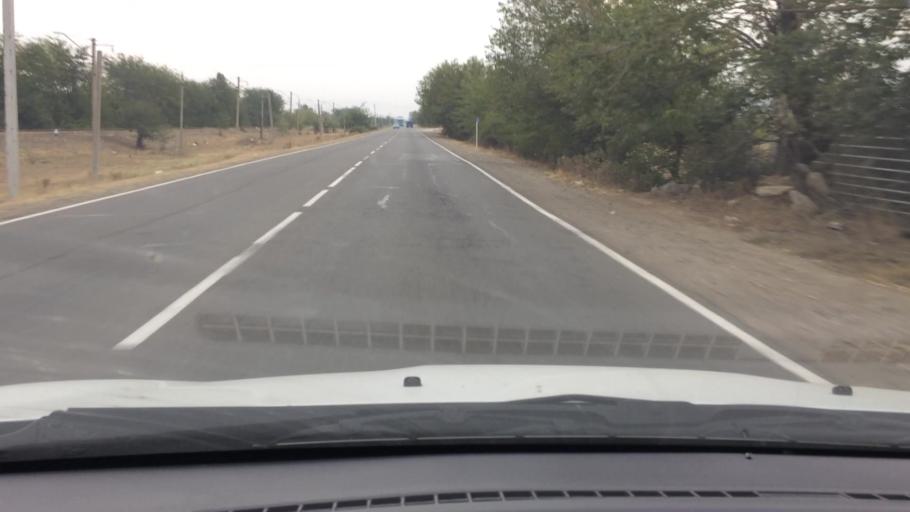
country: GE
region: Kvemo Kartli
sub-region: Marneuli
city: Marneuli
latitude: 41.4578
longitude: 44.8110
